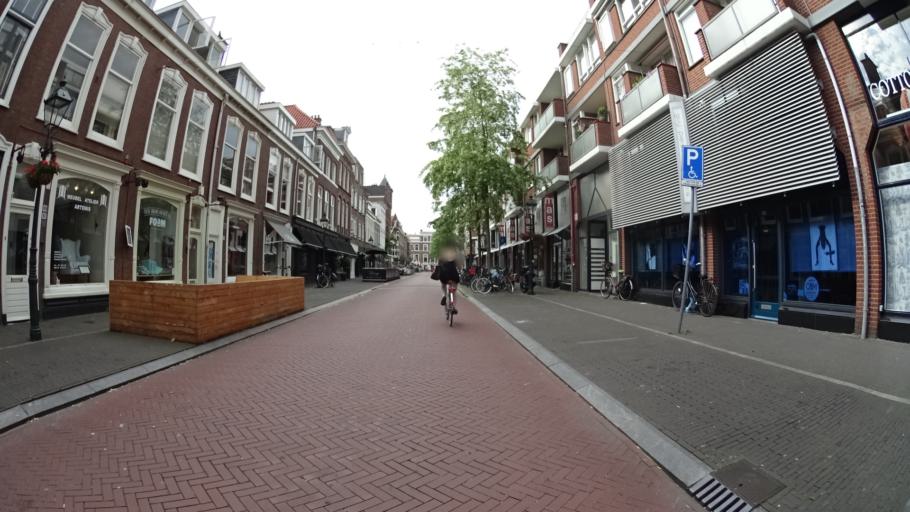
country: NL
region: South Holland
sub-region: Gemeente Den Haag
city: The Hague
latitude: 52.0877
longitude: 4.3105
